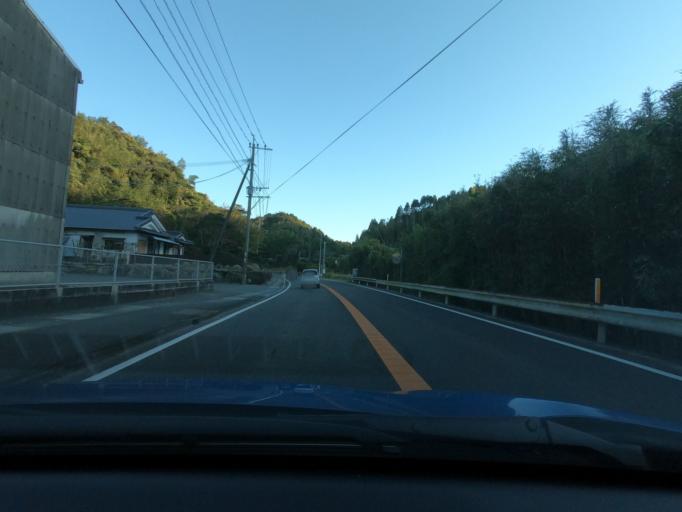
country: JP
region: Kagoshima
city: Satsumasendai
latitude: 31.8524
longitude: 130.2363
